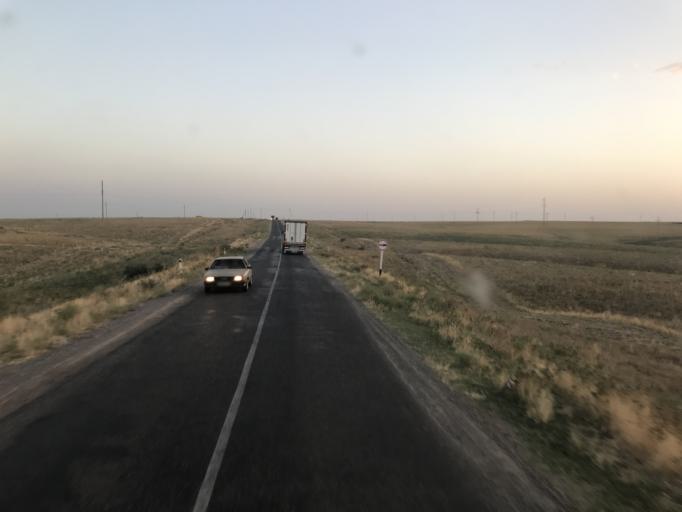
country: UZ
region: Toshkent
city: Chinoz
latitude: 41.3249
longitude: 68.6776
